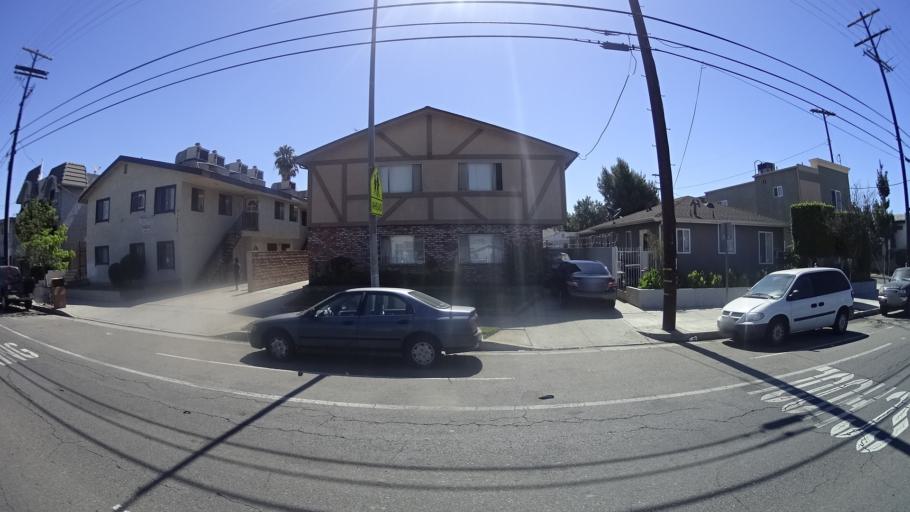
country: US
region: California
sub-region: Los Angeles County
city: Van Nuys
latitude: 34.1953
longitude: -118.4836
